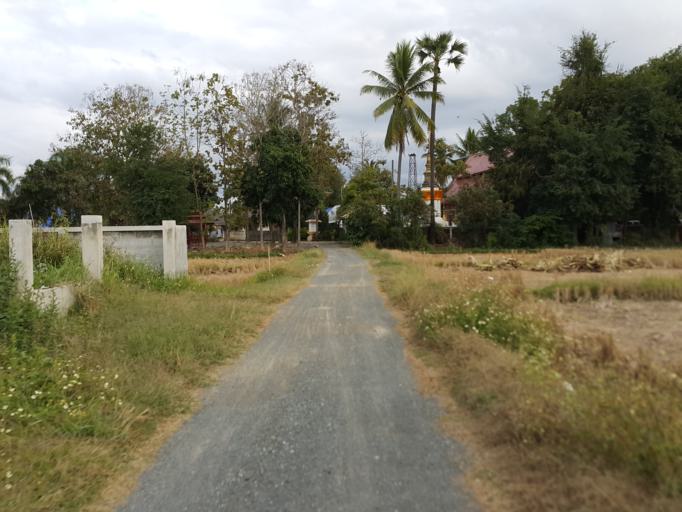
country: TH
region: Chiang Mai
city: San Sai
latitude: 18.8534
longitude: 99.1175
